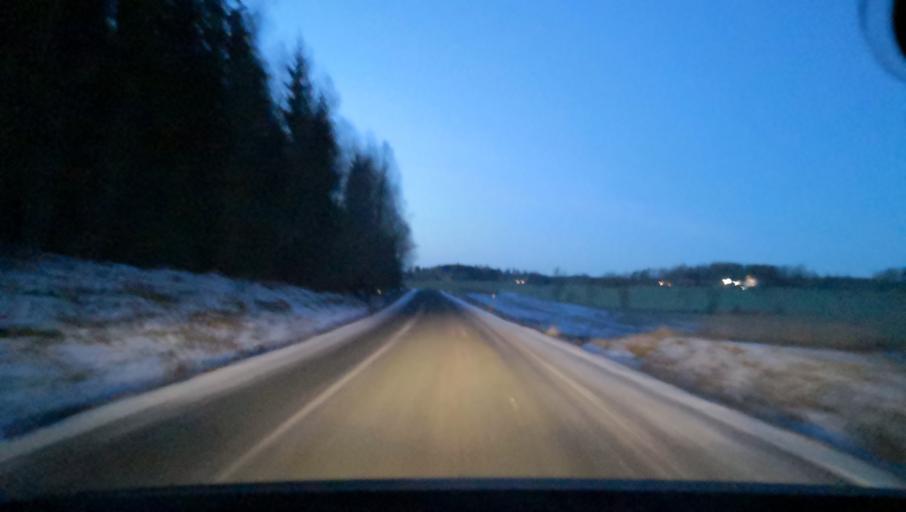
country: SE
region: Soedermanland
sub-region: Katrineholms Kommun
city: Katrineholm
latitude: 59.0744
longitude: 16.3473
